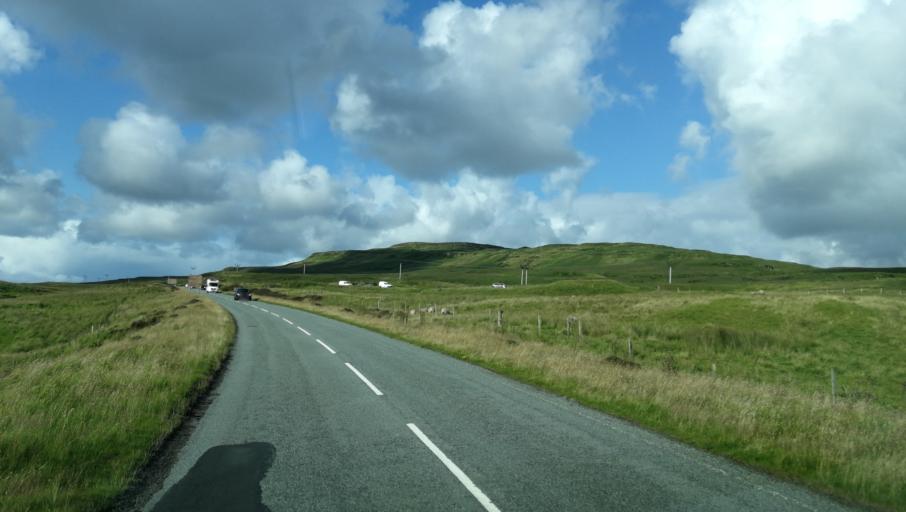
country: GB
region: Scotland
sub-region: Highland
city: Isle of Skye
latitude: 57.4422
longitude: -6.5437
